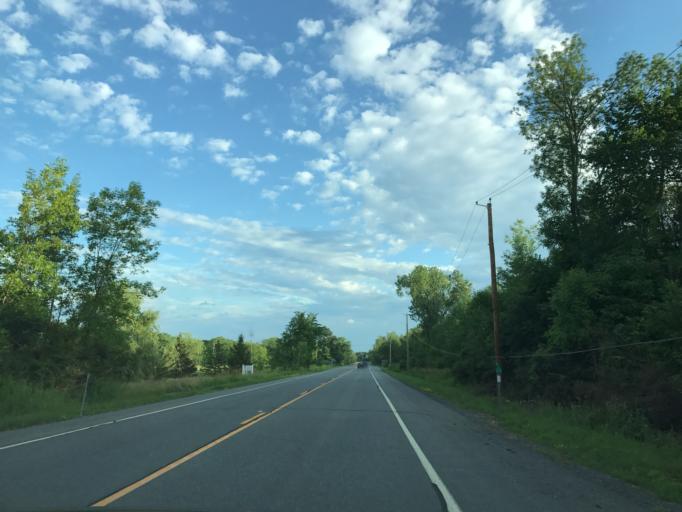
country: US
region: New York
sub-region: Saratoga County
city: Schuylerville
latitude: 43.0215
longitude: -73.5961
